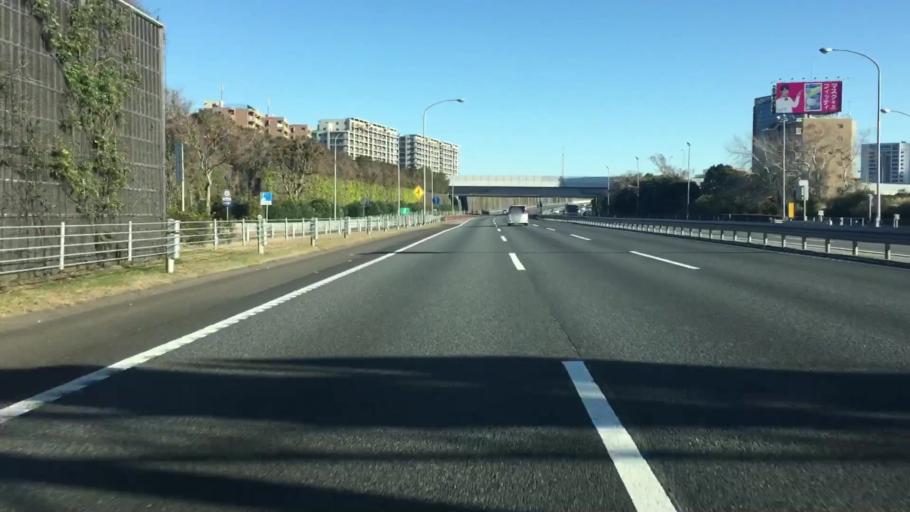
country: JP
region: Chiba
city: Funabashi
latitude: 35.6598
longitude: 140.0305
